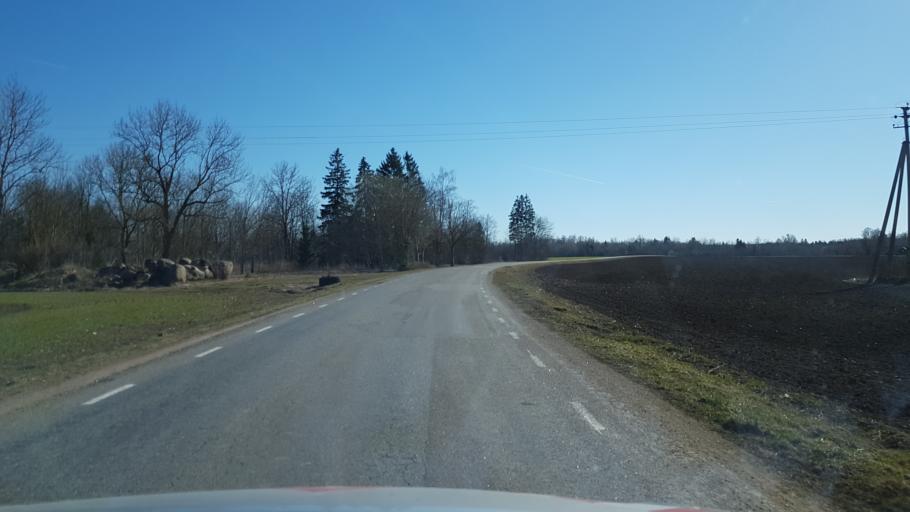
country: EE
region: Laeaene-Virumaa
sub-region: Someru vald
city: Someru
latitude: 59.3746
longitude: 26.4536
